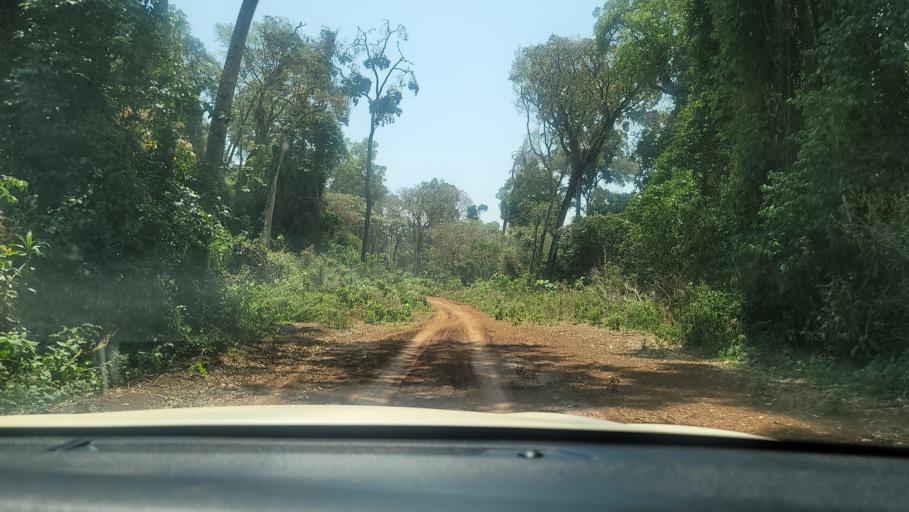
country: ET
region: Southern Nations, Nationalities, and People's Region
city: Bonga
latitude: 7.5450
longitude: 36.1777
